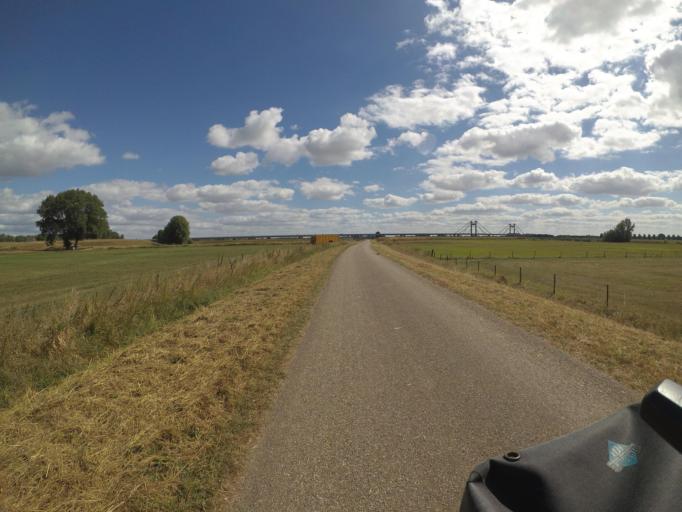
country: NL
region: Gelderland
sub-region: Gemeente Buren
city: Lienden
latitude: 51.8981
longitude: 5.4872
